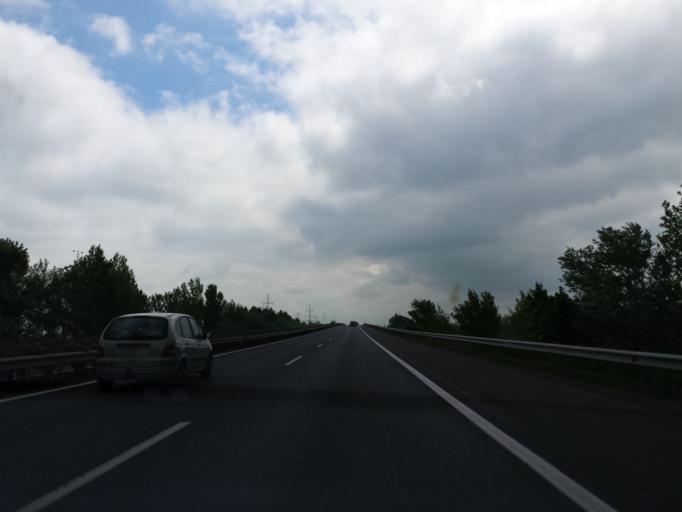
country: HU
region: Gyor-Moson-Sopron
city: Abda
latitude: 47.6689
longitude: 17.5692
